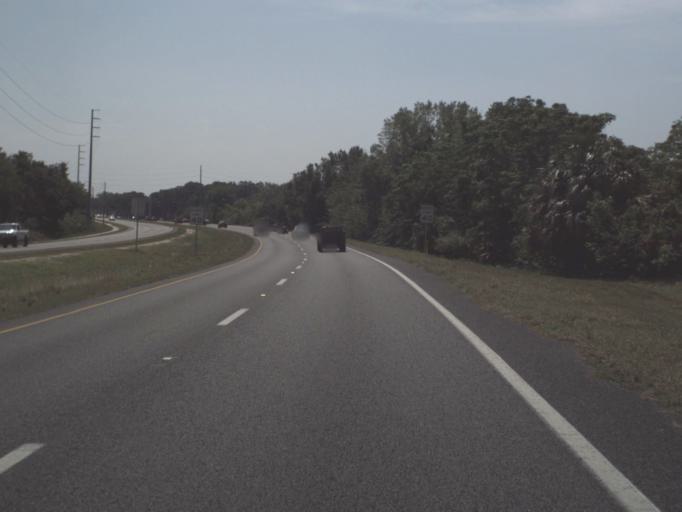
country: US
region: Florida
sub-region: Lake County
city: Eustis
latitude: 28.8692
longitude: -81.6884
